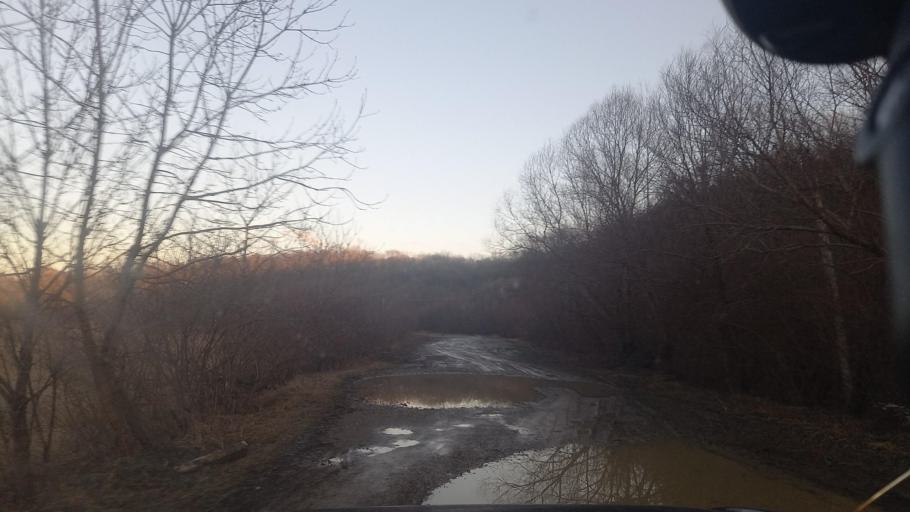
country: RU
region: Krasnodarskiy
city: Smolenskaya
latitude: 44.7642
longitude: 38.7964
